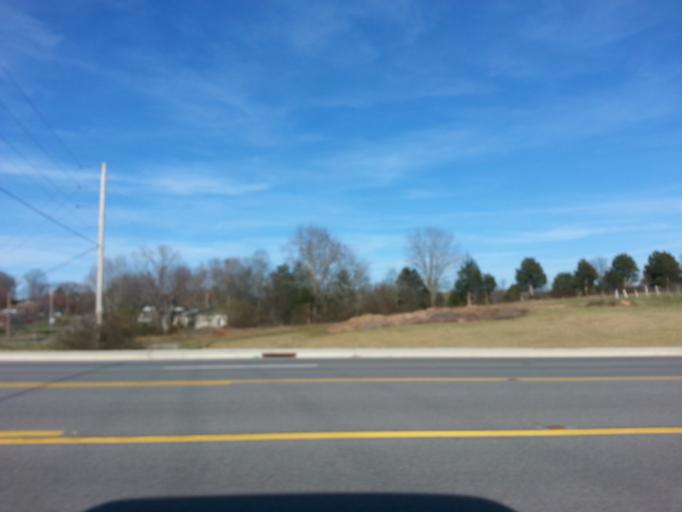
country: US
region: Tennessee
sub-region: Warren County
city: McMinnville
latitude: 35.7014
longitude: -85.8280
